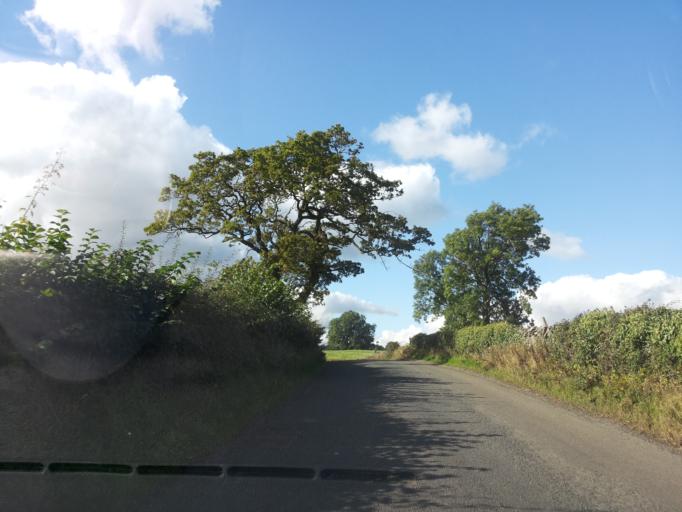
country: GB
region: England
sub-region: North Yorkshire
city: Leyburn
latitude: 54.2765
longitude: -1.8298
